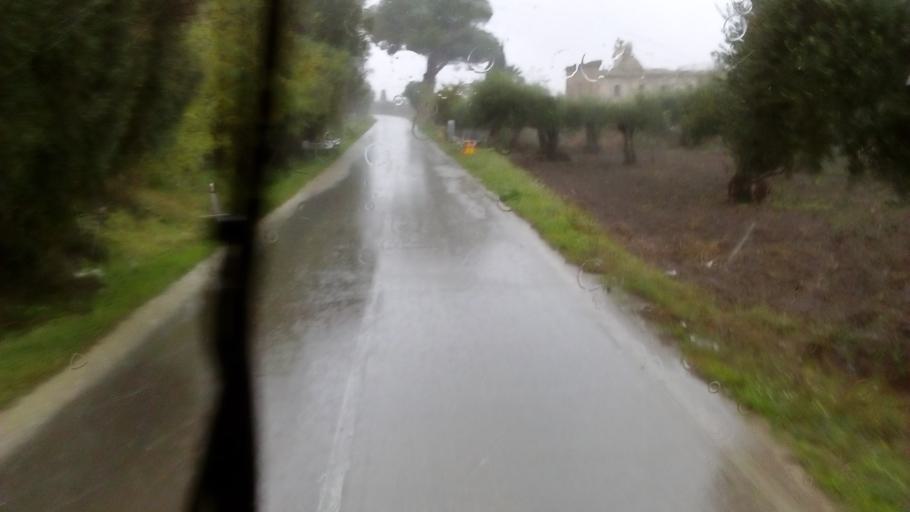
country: IT
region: Sicily
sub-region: Enna
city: Pietraperzia
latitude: 37.4207
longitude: 14.1665
